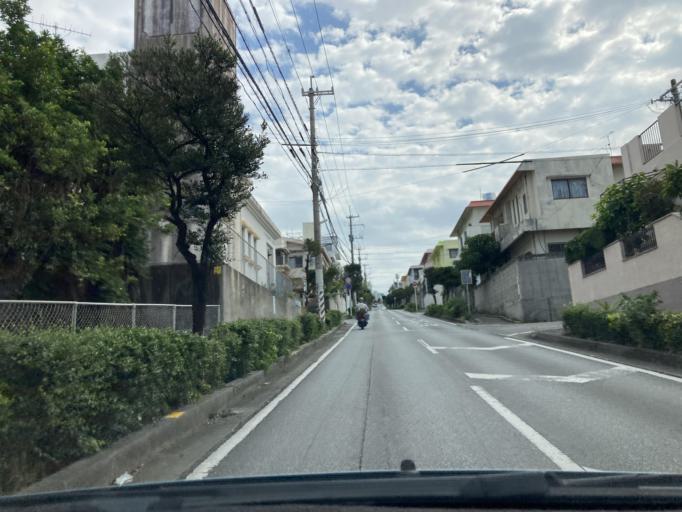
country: JP
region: Okinawa
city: Tomigusuku
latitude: 26.1894
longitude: 127.6938
